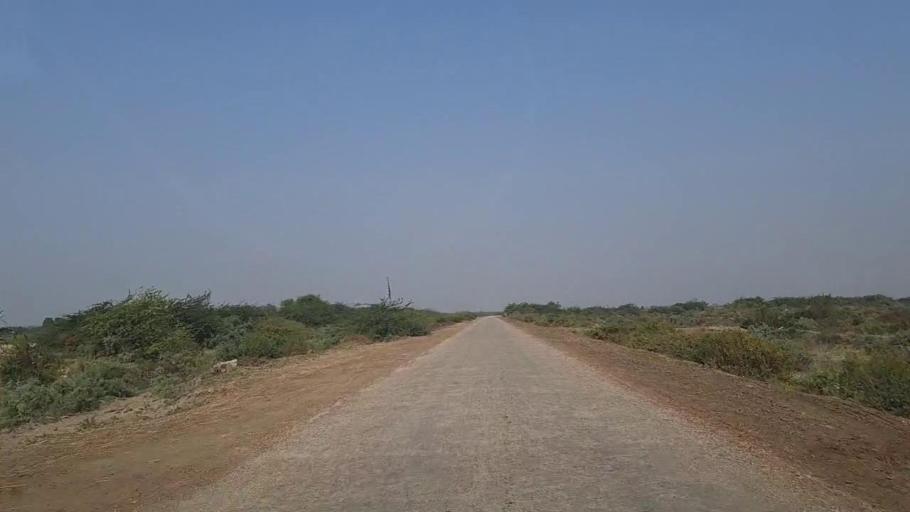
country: PK
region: Sindh
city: Keti Bandar
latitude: 24.2369
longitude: 67.6832
